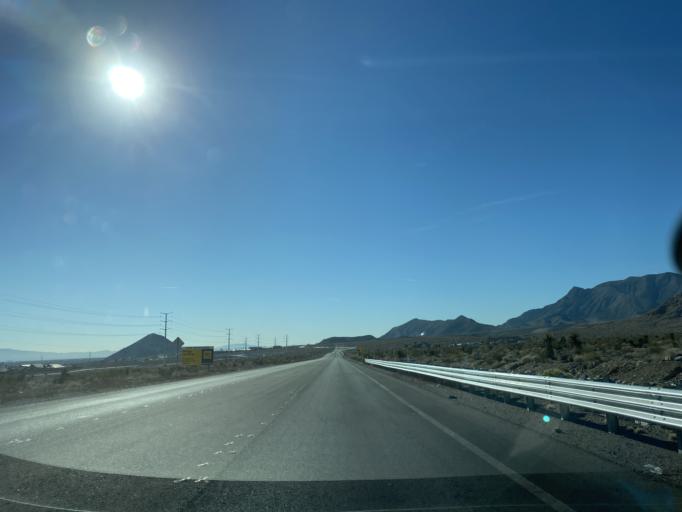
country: US
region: Nevada
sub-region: Clark County
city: Summerlin South
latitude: 36.2726
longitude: -115.3300
